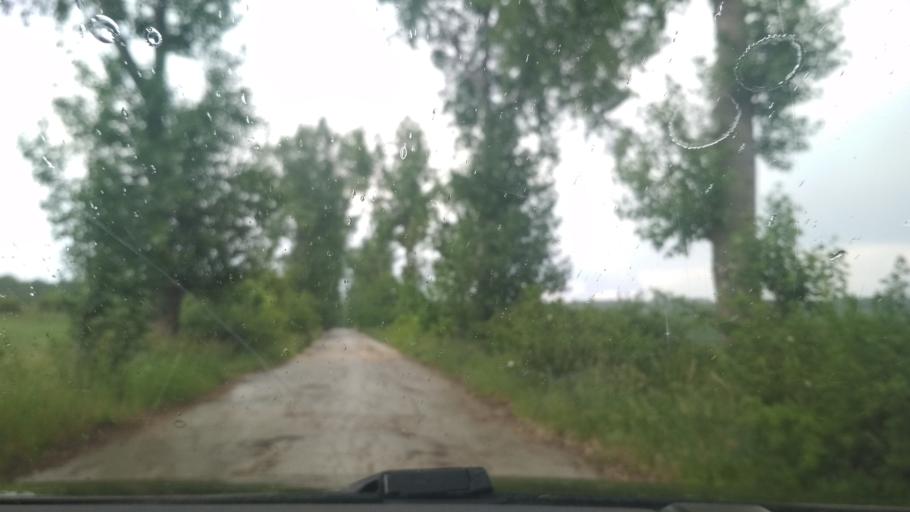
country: MD
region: Singerei
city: Biruinta
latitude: 47.7453
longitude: 28.1385
